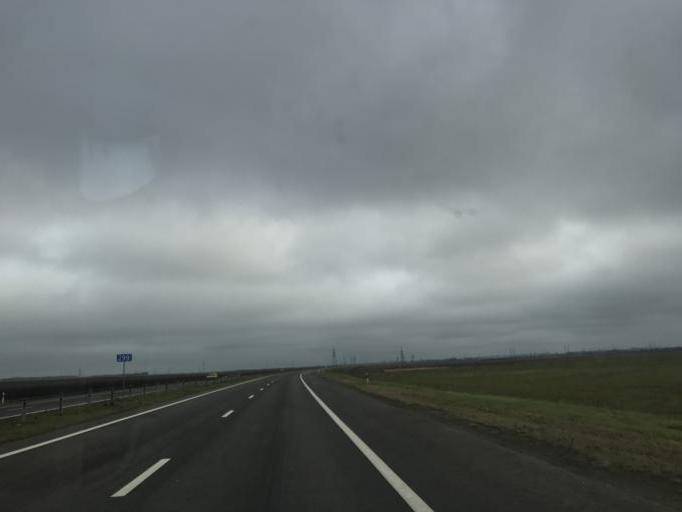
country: BY
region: Gomel
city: Kastsyukowka
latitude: 52.4959
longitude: 30.8842
